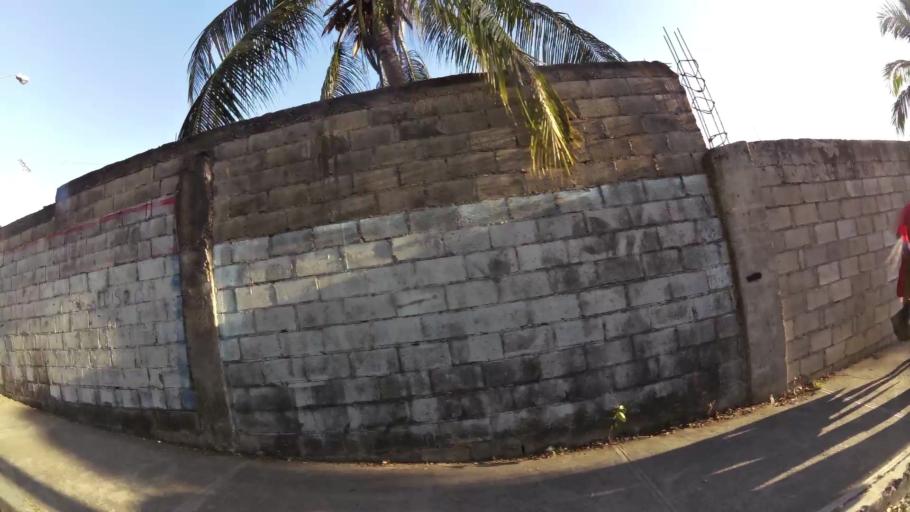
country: DO
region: Nacional
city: Santo Domingo
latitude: 18.4879
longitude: -69.9654
